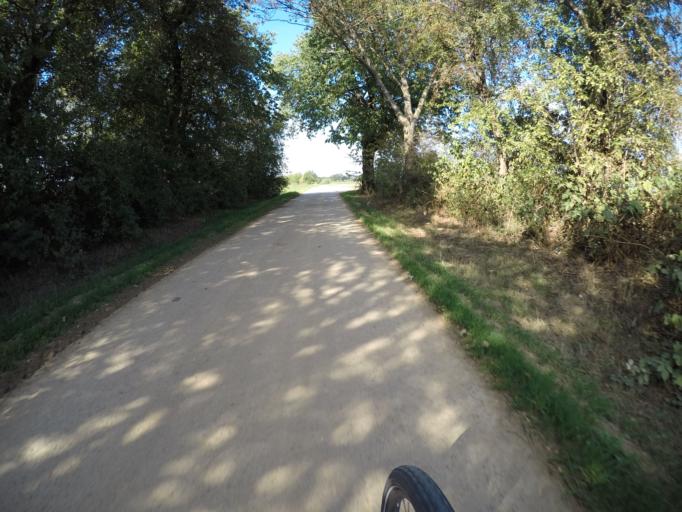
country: DE
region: Baden-Wuerttemberg
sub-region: Regierungsbezirk Stuttgart
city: Neuhausen auf den Fildern
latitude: 48.6957
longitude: 9.2803
